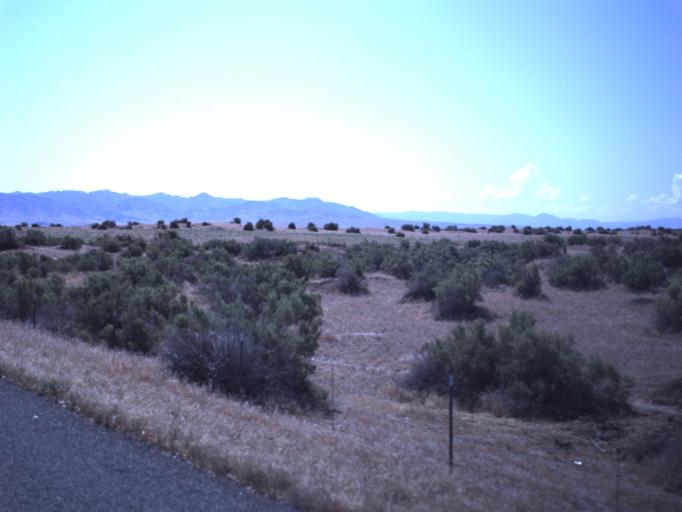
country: US
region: Utah
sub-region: Millard County
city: Delta
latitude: 39.4740
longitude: -112.4785
